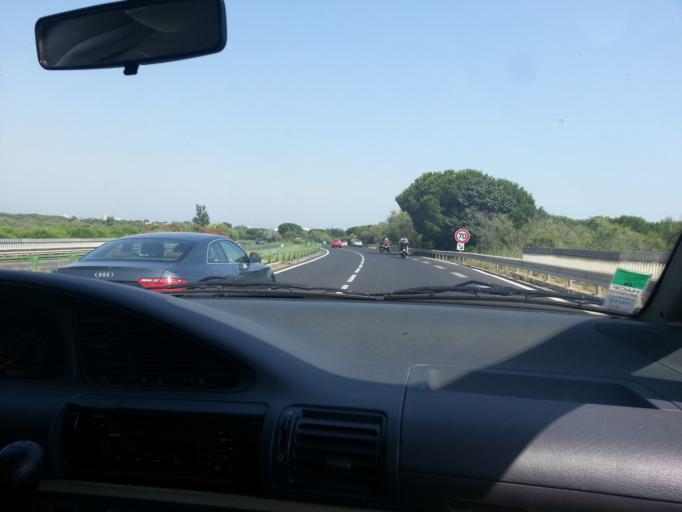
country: FR
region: Languedoc-Roussillon
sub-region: Departement de l'Herault
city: Perols
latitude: 43.5497
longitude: 3.9805
